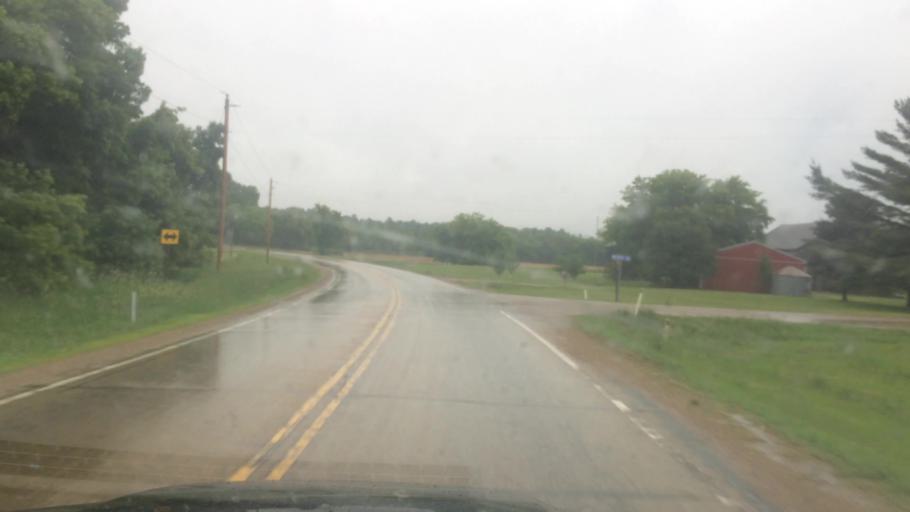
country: US
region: Wisconsin
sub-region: Waupaca County
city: Marion
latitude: 44.6104
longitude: -88.8802
